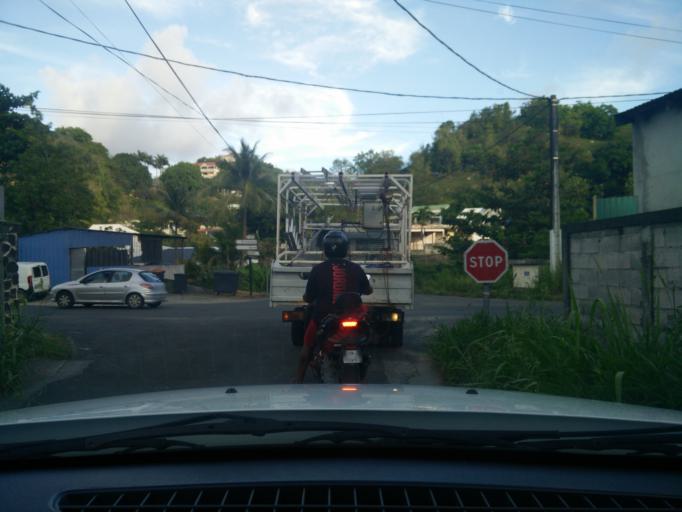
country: GP
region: Guadeloupe
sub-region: Guadeloupe
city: Les Abymes
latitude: 16.2481
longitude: -61.4936
